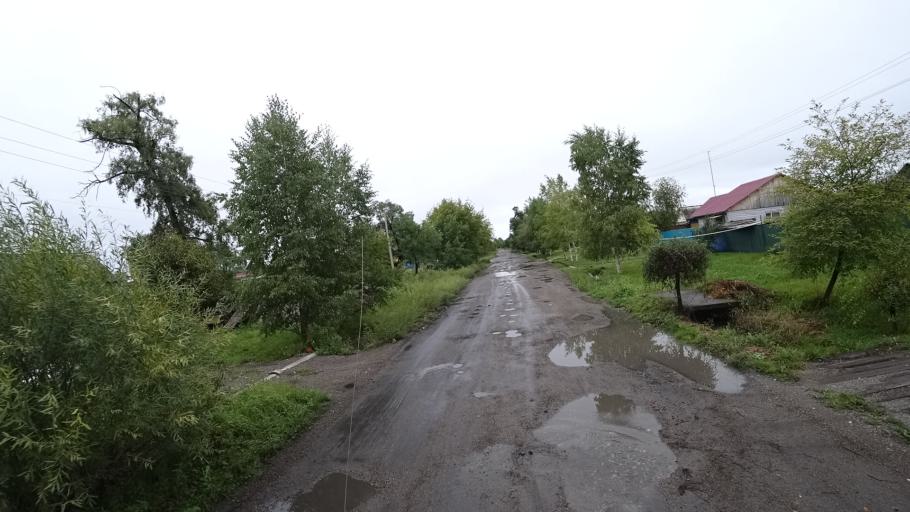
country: RU
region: Primorskiy
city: Monastyrishche
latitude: 44.1985
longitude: 132.4677
